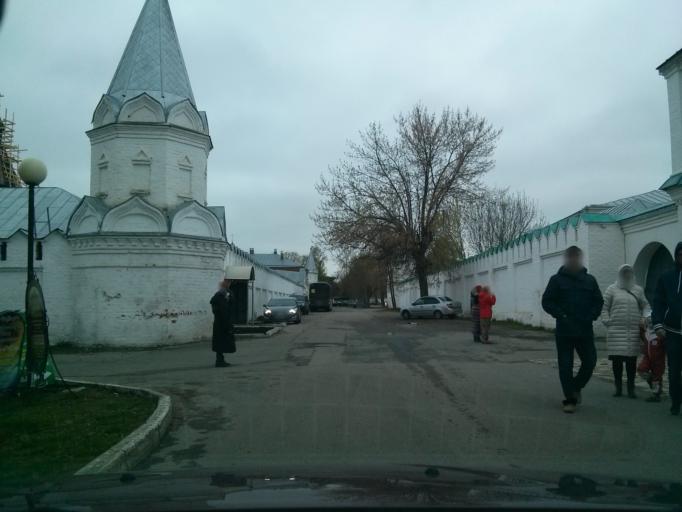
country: RU
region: Vladimir
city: Murom
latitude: 55.5822
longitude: 42.0541
